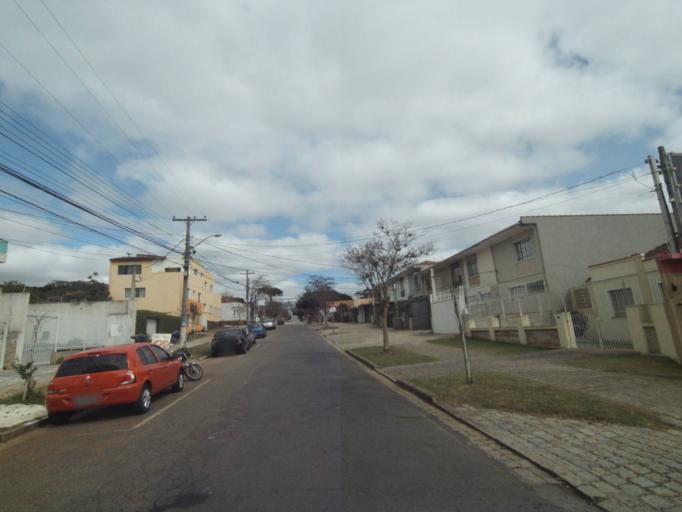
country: BR
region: Parana
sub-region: Curitiba
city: Curitiba
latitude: -25.4510
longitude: -49.2752
